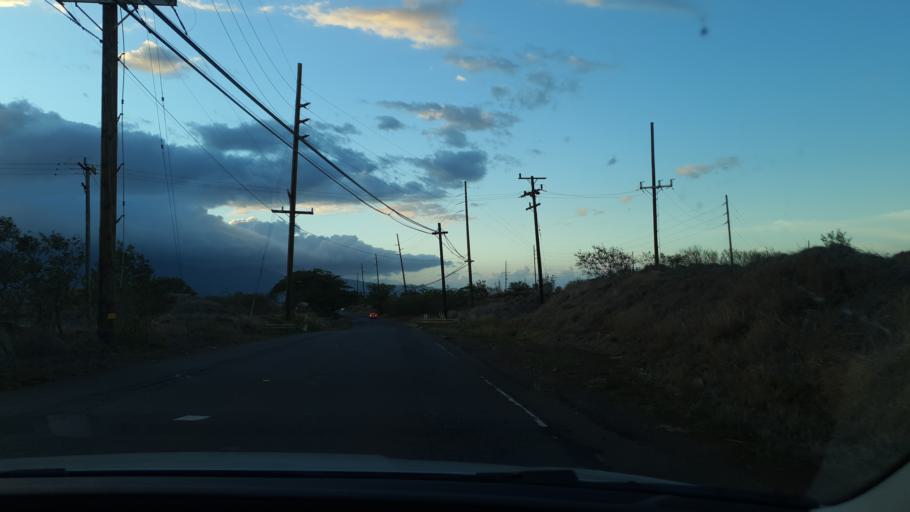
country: US
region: Hawaii
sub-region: Maui County
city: Kahului
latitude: 20.8700
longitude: -156.4368
